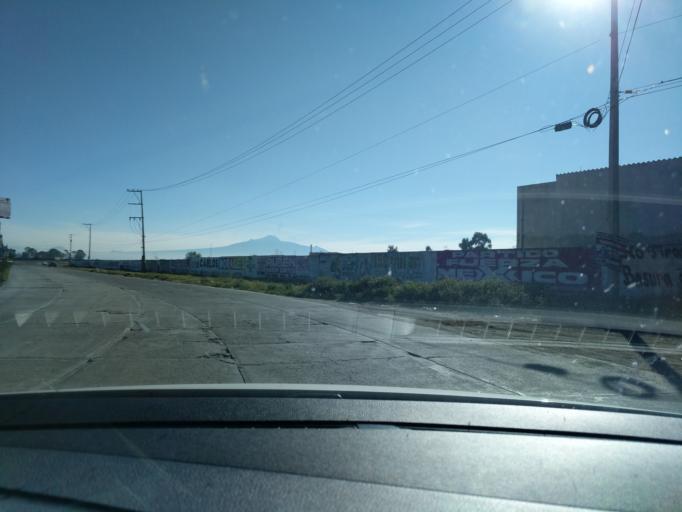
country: MX
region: Puebla
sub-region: Huejotzingo
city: Los Encinos
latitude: 19.1714
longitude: -98.3769
